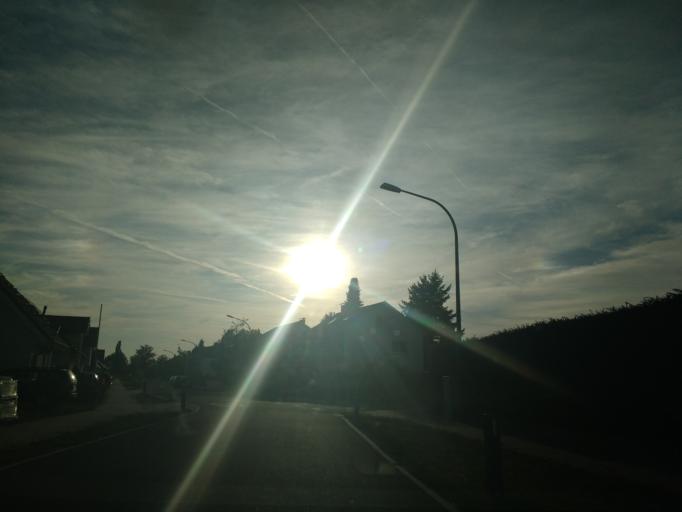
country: DE
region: North Rhine-Westphalia
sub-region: Regierungsbezirk Detmold
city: Hovelhof
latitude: 51.8693
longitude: 8.6825
